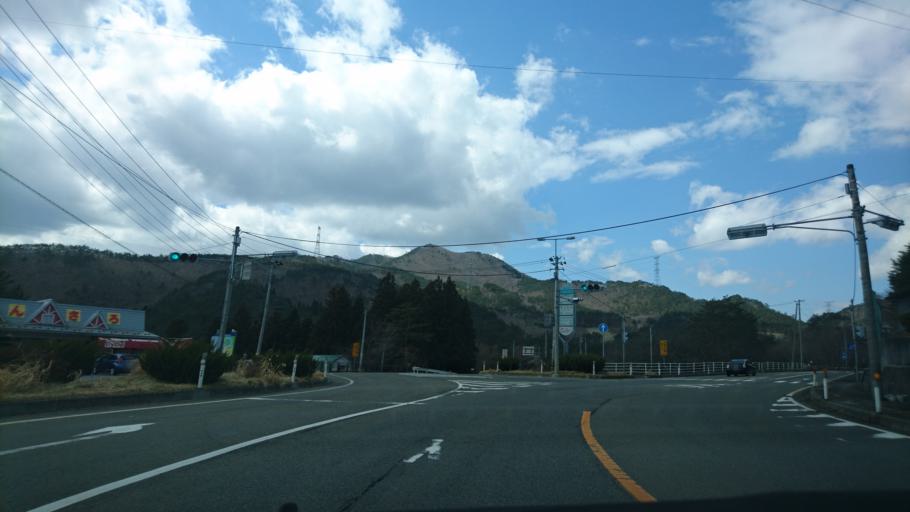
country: JP
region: Iwate
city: Tono
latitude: 39.3111
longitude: 141.3733
